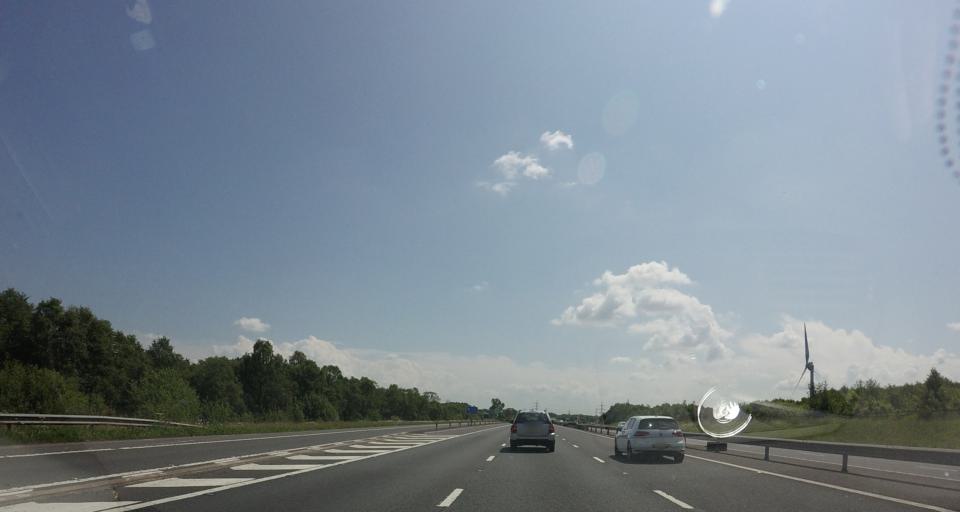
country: GB
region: England
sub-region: Cumbria
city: Carlisle
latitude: 54.9541
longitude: -2.9828
